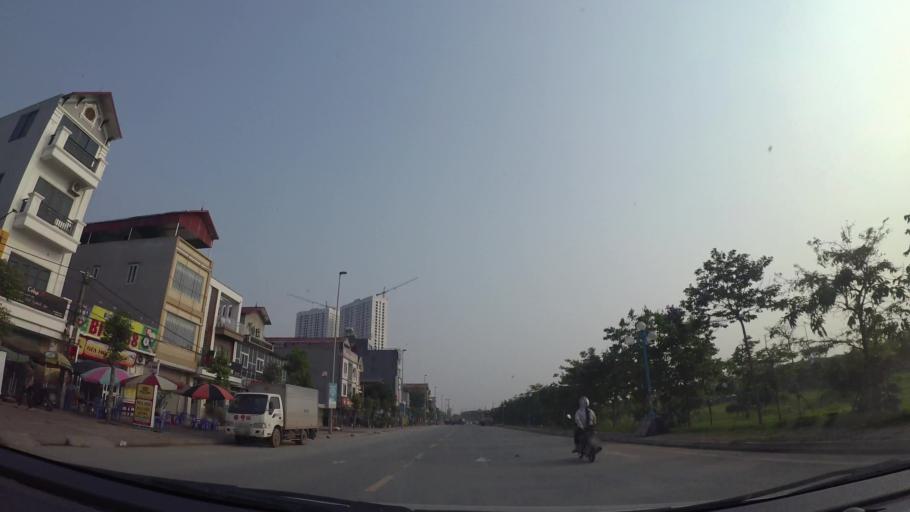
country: VN
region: Ha Noi
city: Dong Anh
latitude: 21.1168
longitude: 105.8282
